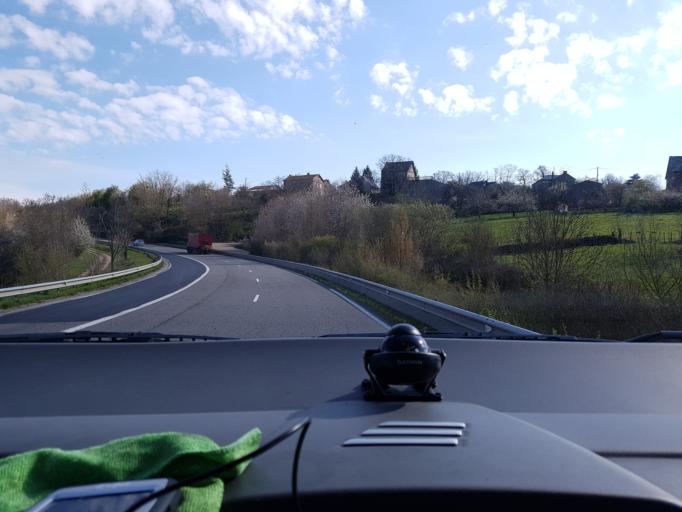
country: FR
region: Midi-Pyrenees
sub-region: Departement de l'Aveyron
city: Moyrazes
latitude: 44.3776
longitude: 2.4431
